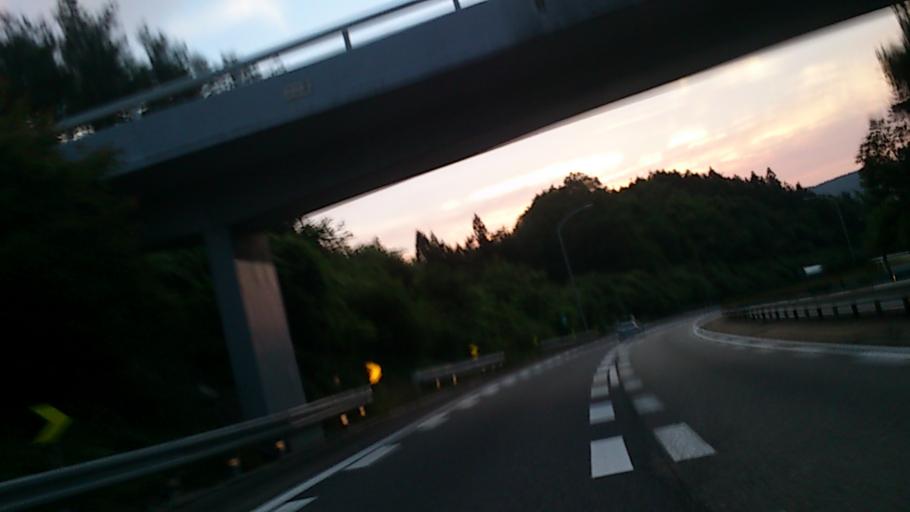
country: JP
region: Gifu
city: Nakatsugawa
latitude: 35.5129
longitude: 137.5768
